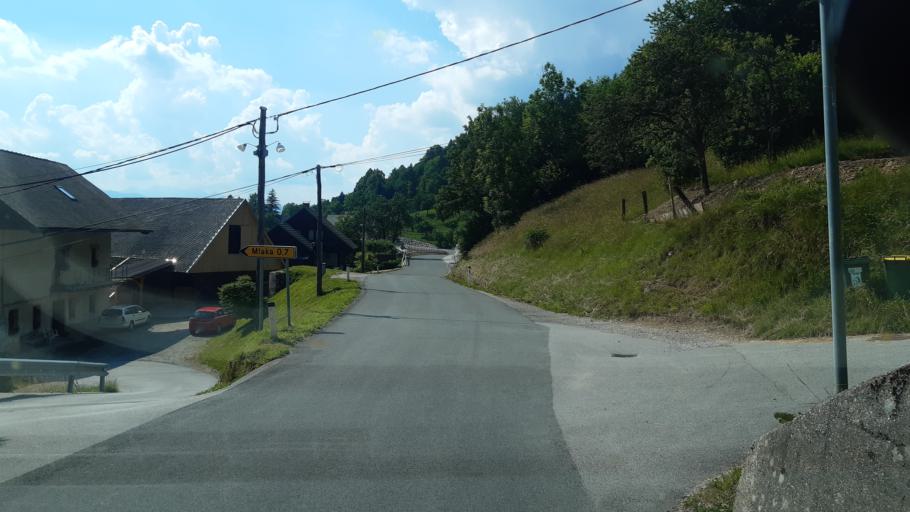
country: SI
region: Trzic
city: Bistrica pri Trzicu
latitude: 46.3624
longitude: 14.2408
